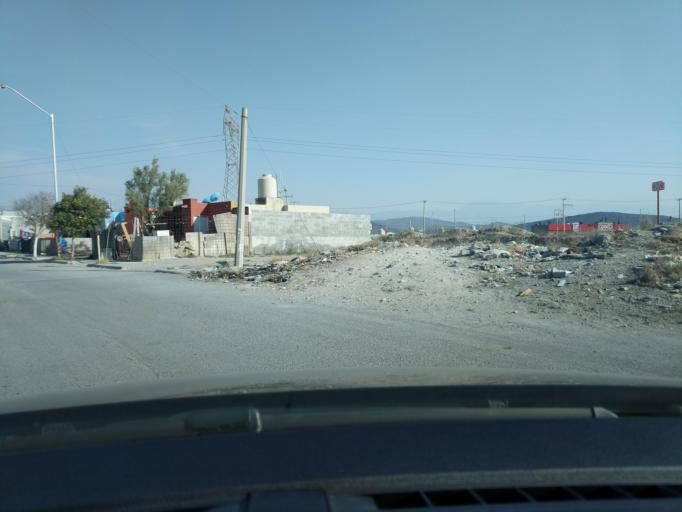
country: MX
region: Coahuila
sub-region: Ramos Arizpe
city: Ramos Arizpe
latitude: 25.5459
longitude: -100.9679
